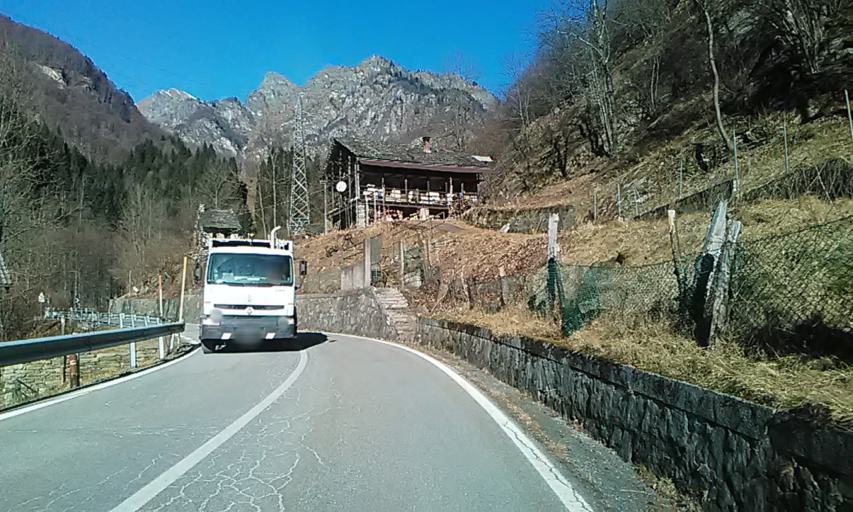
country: IT
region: Piedmont
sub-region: Provincia di Vercelli
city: Rimasco
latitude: 45.8512
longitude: 8.0657
